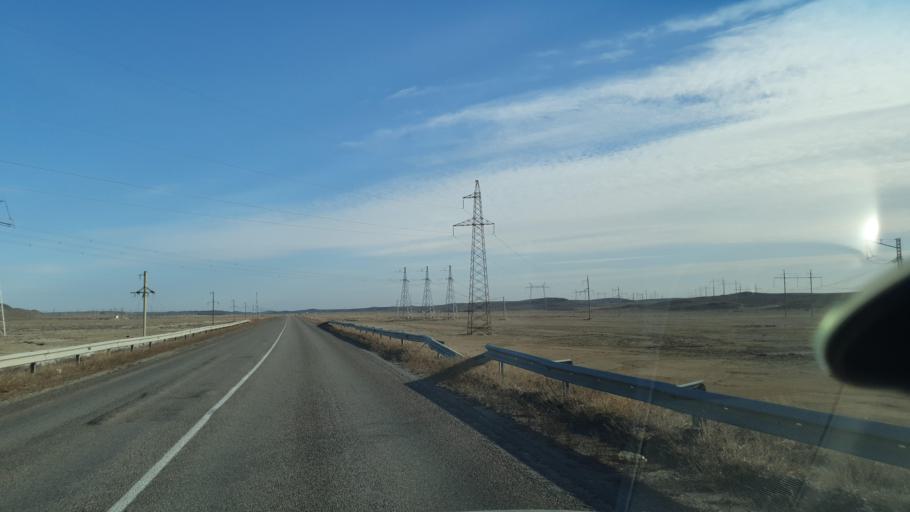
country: KZ
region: Zhambyl
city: Mynaral
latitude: 45.5623
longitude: 73.4267
